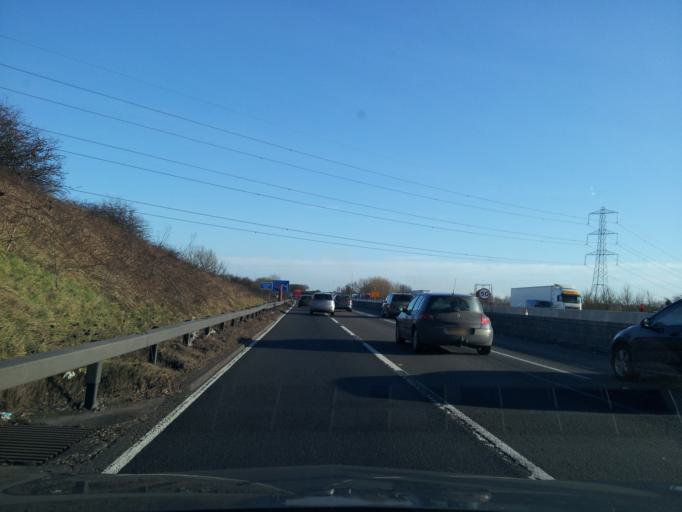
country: GB
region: England
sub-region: Northamptonshire
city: Bugbrooke
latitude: 52.2396
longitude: -1.0461
